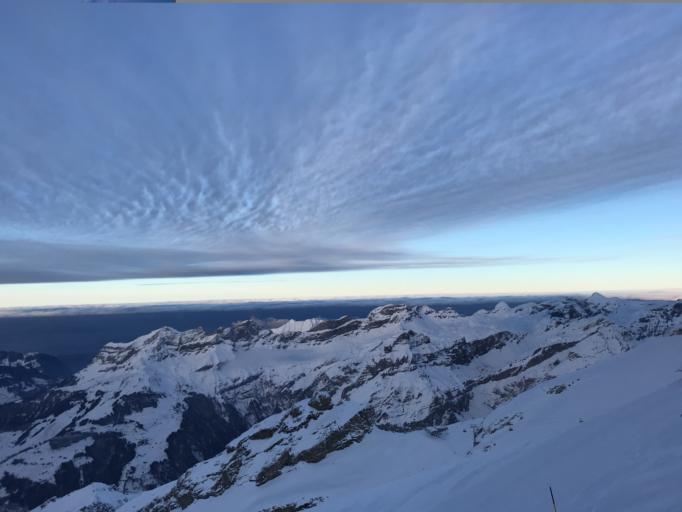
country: CH
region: Obwalden
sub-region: Obwalden
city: Engelberg
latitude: 46.7708
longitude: 8.4233
